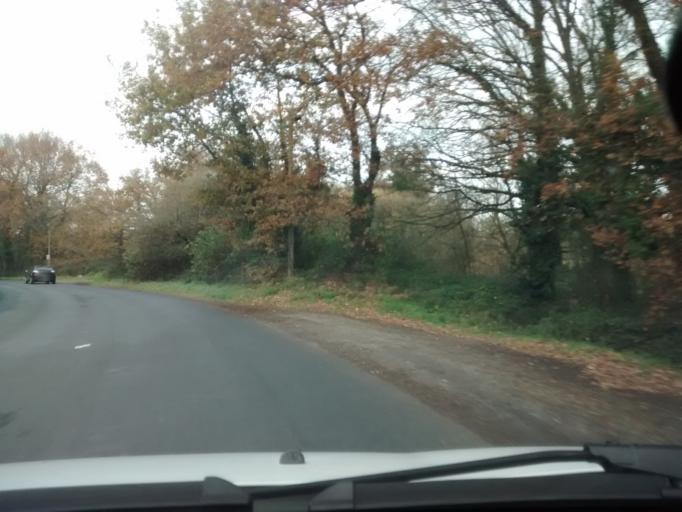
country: FR
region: Brittany
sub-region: Departement d'Ille-et-Vilaine
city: Saint-Jacques-de-la-Lande
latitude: 48.0851
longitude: -1.7316
